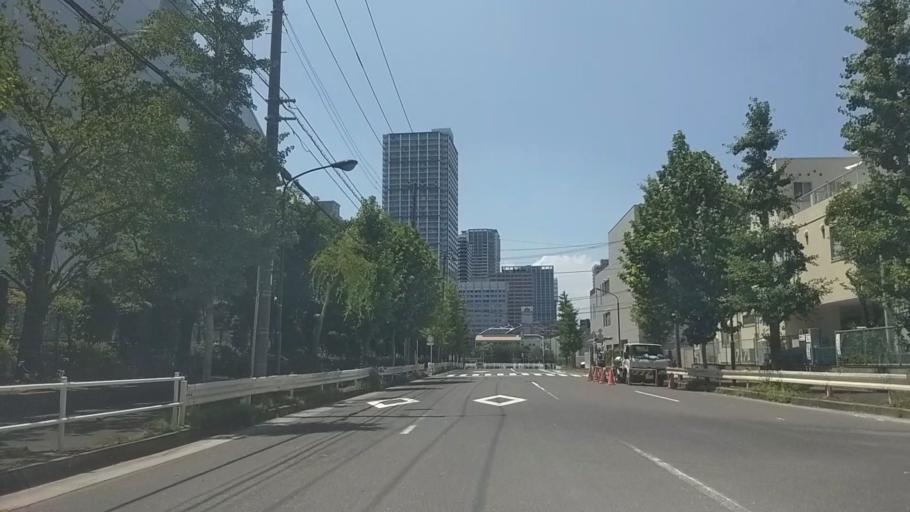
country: JP
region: Tokyo
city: Tokyo
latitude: 35.6321
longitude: 139.7563
